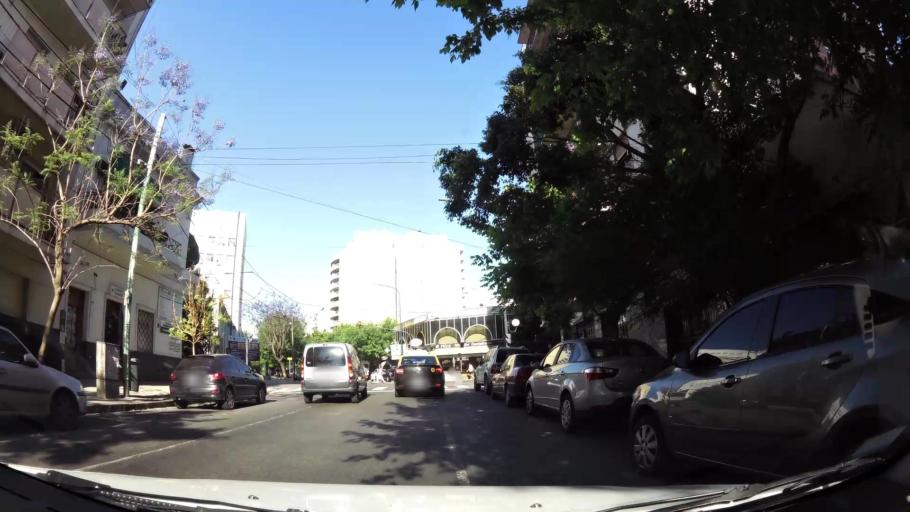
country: AR
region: Buenos Aires F.D.
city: Villa Santa Rita
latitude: -34.6147
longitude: -58.4399
